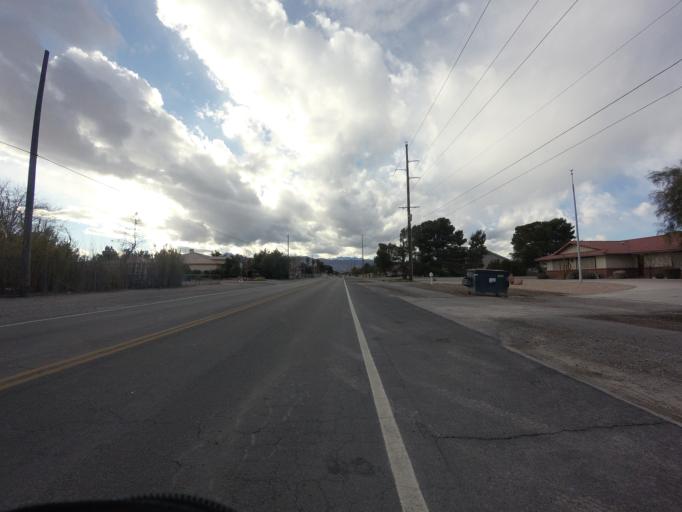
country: US
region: Nevada
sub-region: Clark County
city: Las Vegas
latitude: 36.2688
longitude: -115.2312
